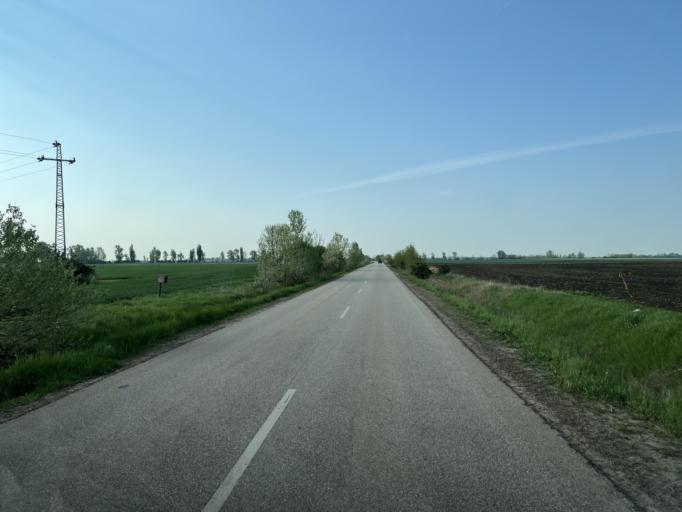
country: HU
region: Pest
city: Abony
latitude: 47.1215
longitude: 20.0142
